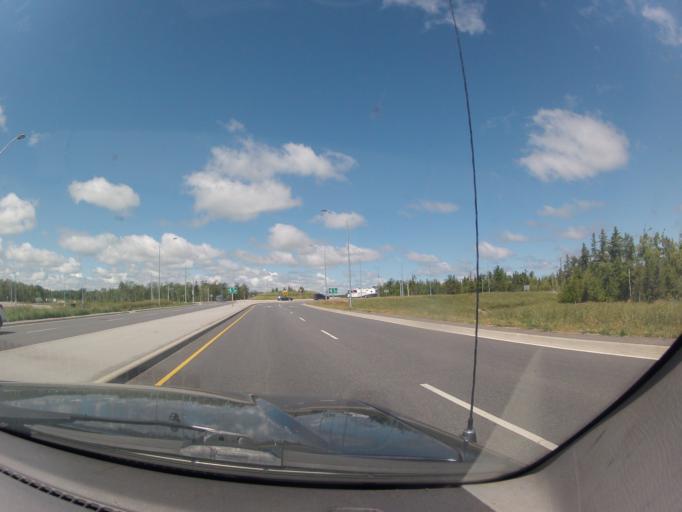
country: CA
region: Ontario
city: Collingwood
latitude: 44.4616
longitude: -80.1117
